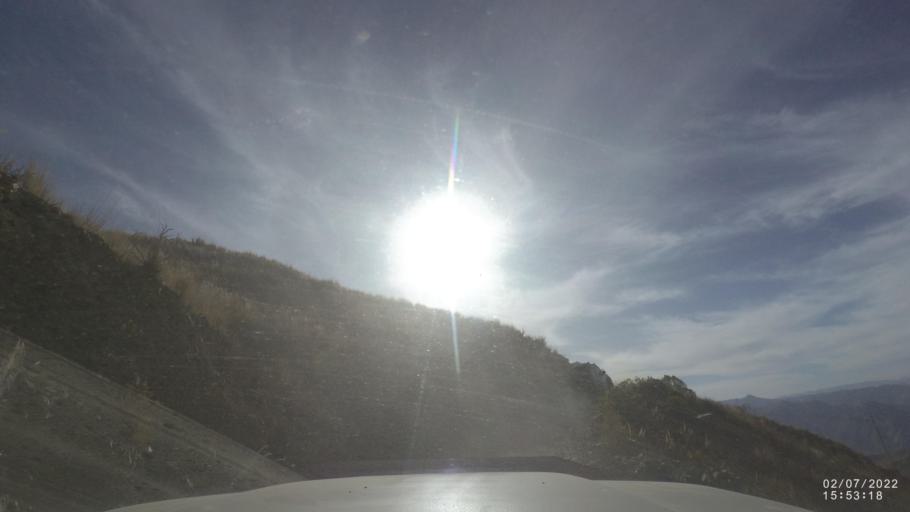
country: BO
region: Cochabamba
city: Irpa Irpa
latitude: -17.9089
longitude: -66.4161
